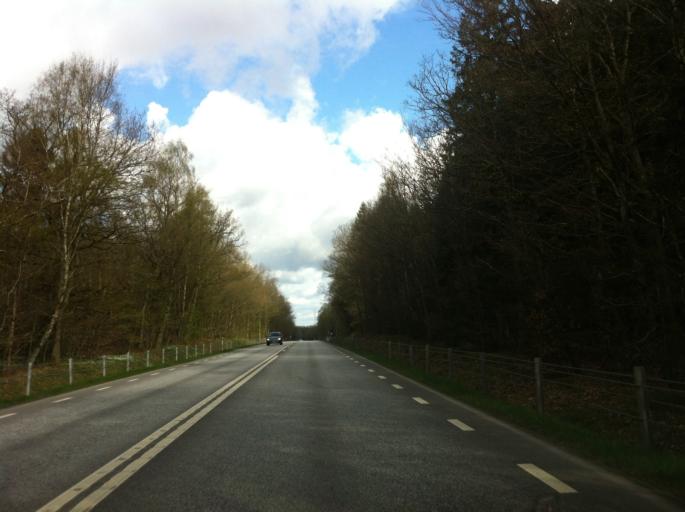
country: SE
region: Skane
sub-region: Horby Kommun
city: Hoerby
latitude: 55.8882
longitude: 13.6281
